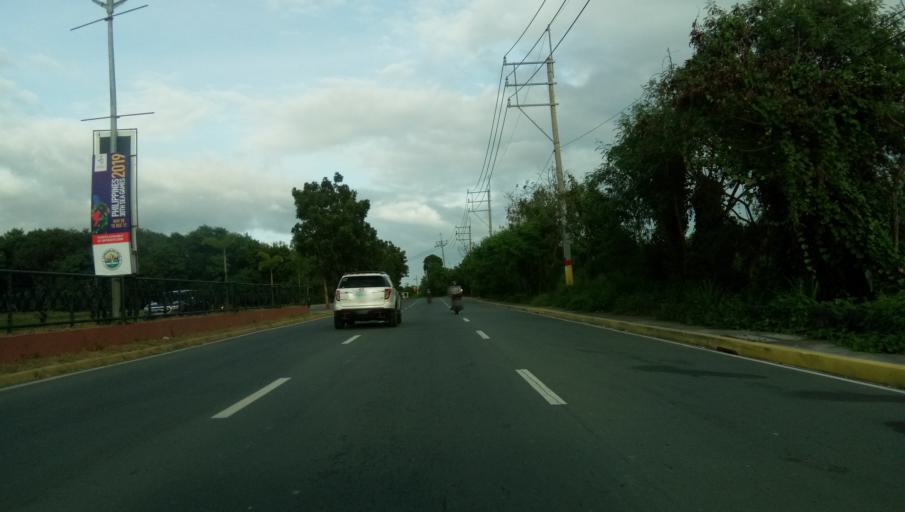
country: PH
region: Calabarzon
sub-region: Province of Cavite
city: Dasmarinas
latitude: 14.3773
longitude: 120.9515
